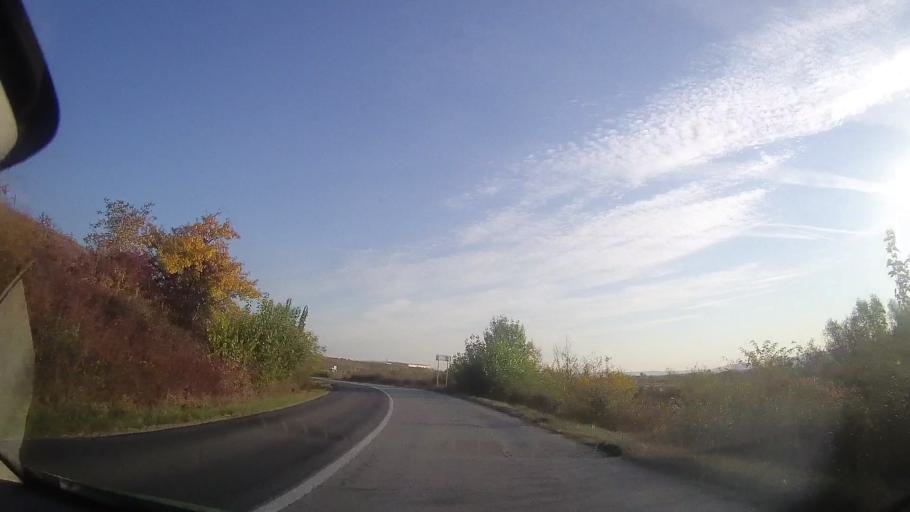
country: RO
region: Timis
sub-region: Comuna Fibis
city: Fibis
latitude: 45.9474
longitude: 21.4094
